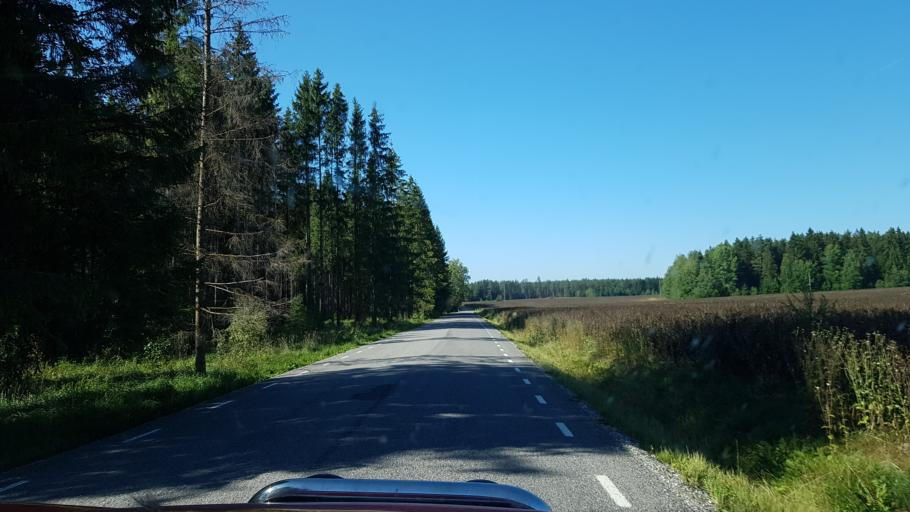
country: EE
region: Polvamaa
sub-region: Polva linn
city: Polva
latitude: 58.2112
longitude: 27.1557
